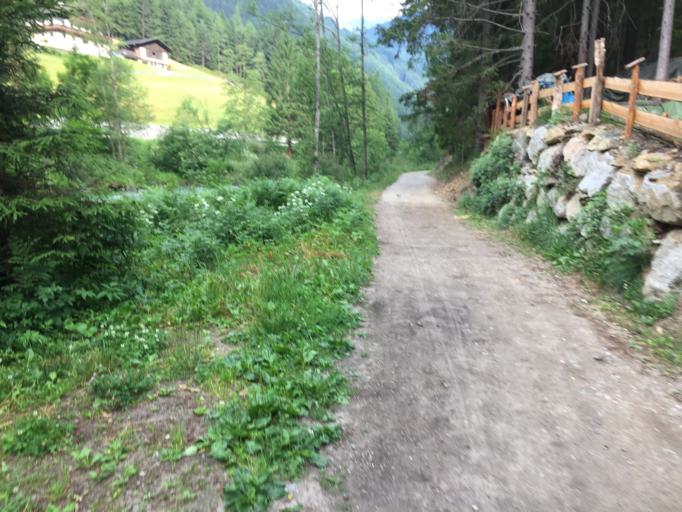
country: IT
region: Trentino-Alto Adige
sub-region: Bolzano
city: Campo Tures
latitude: 46.9380
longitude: 11.9338
